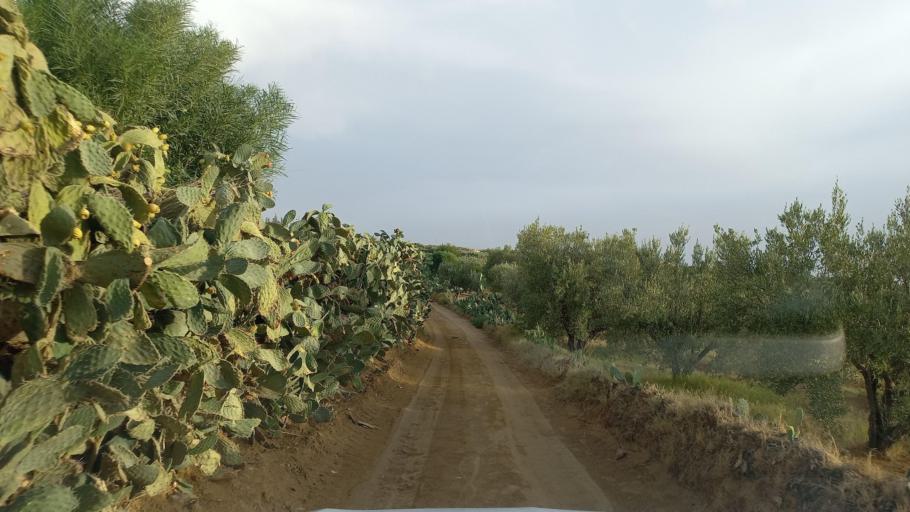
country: TN
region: Al Qasrayn
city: Kasserine
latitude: 35.2197
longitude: 9.0522
